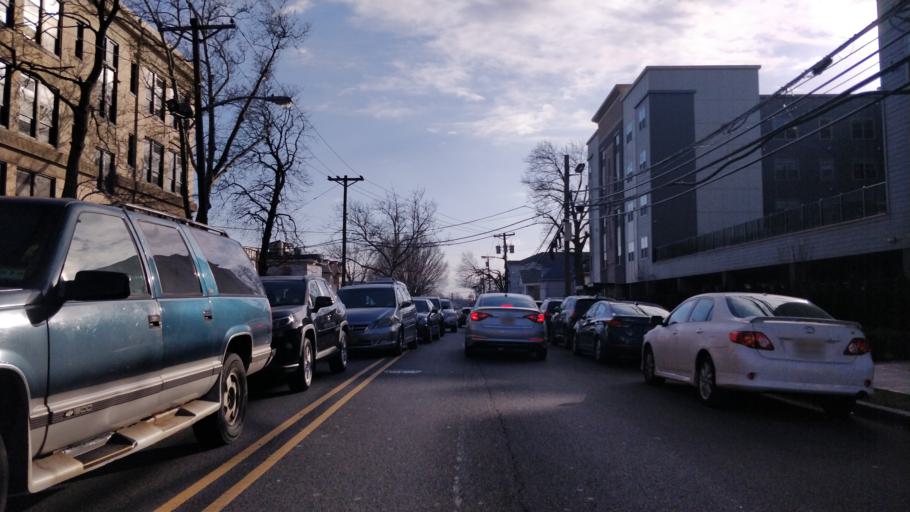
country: US
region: New Jersey
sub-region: Union County
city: Elizabeth
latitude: 40.6575
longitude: -74.2155
